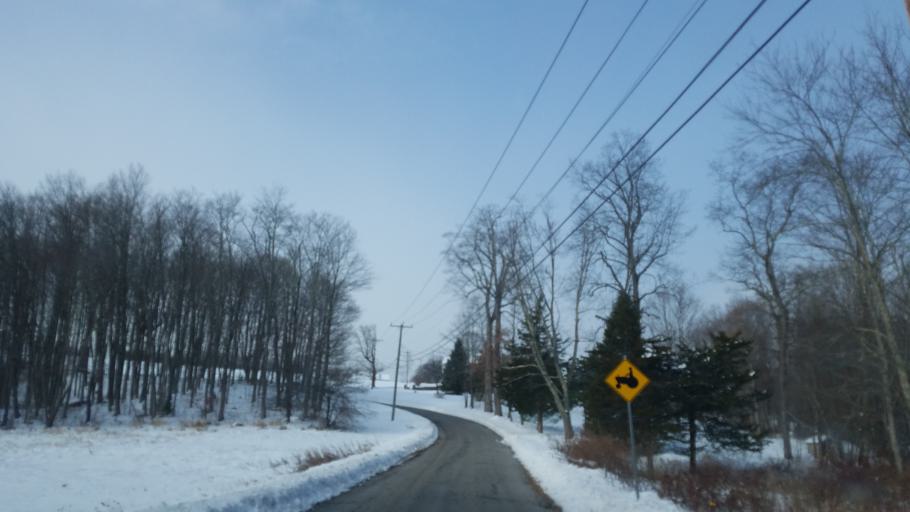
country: US
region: Connecticut
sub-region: Hartford County
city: Canton Valley
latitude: 41.8465
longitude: -72.9009
